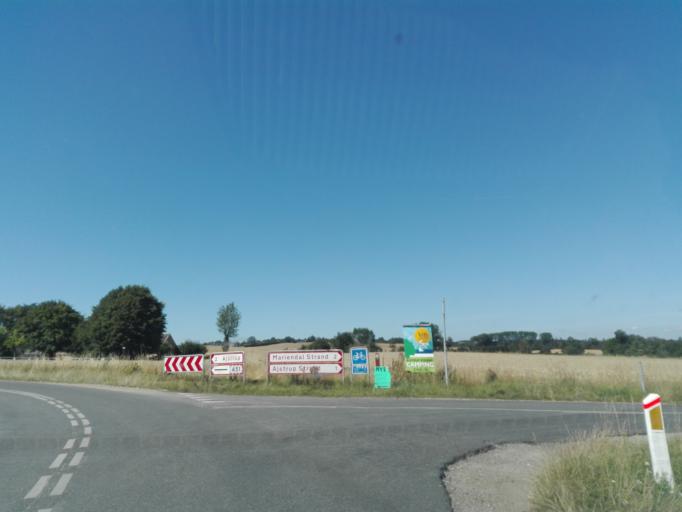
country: DK
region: Central Jutland
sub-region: Arhus Kommune
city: Beder
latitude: 56.0295
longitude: 10.2581
